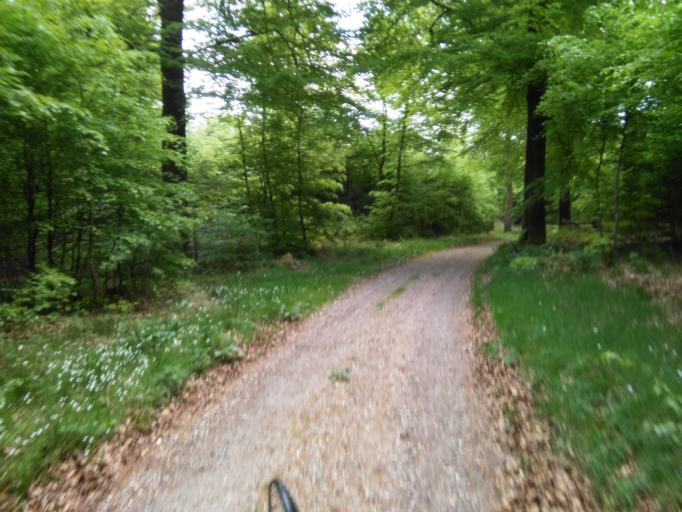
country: DK
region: Central Jutland
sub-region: Horsens Kommune
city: Braedstrup
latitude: 56.0491
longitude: 9.6219
